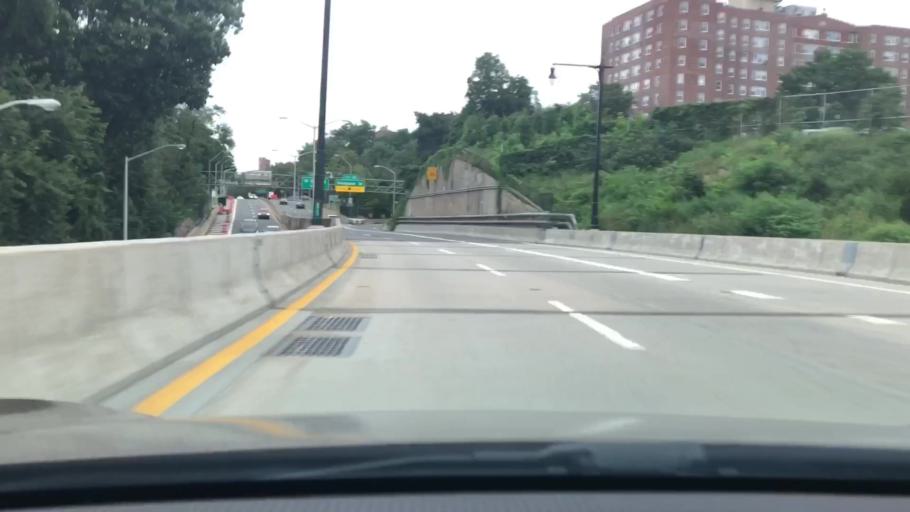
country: US
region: New York
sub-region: New York County
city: Inwood
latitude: 40.8803
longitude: -73.9195
